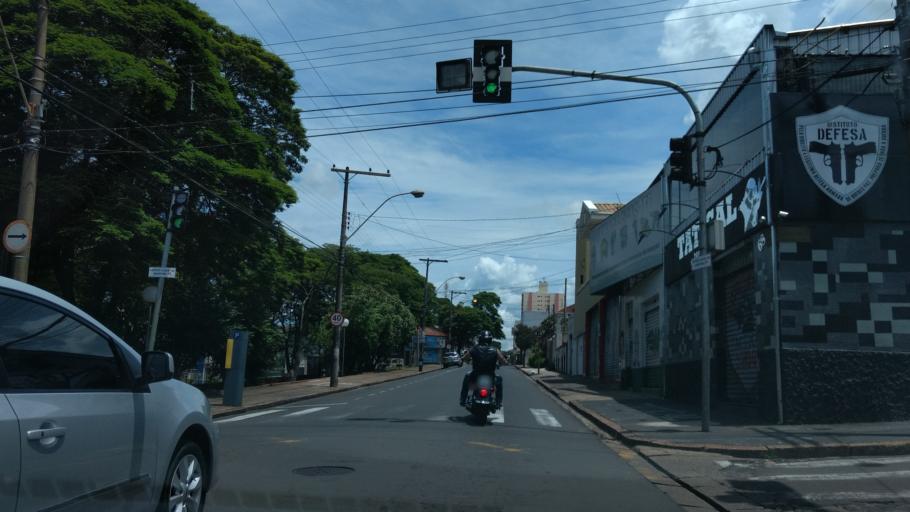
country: BR
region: Sao Paulo
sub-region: Botucatu
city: Botucatu
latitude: -22.8828
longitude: -48.4415
